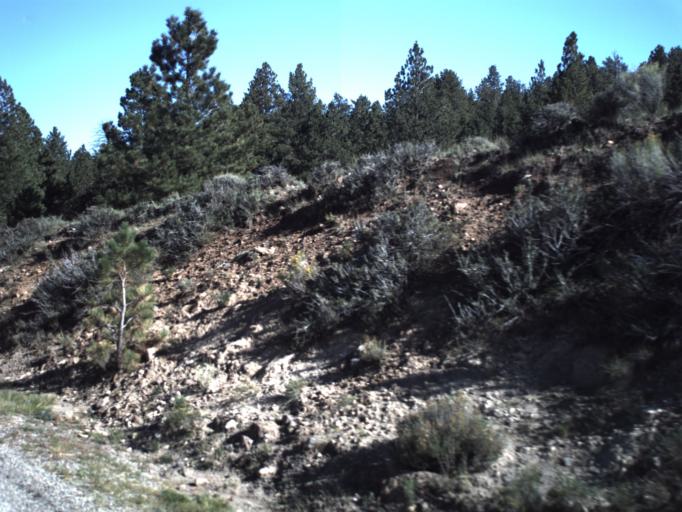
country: US
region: Utah
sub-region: Garfield County
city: Panguitch
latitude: 37.7465
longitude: -112.5826
